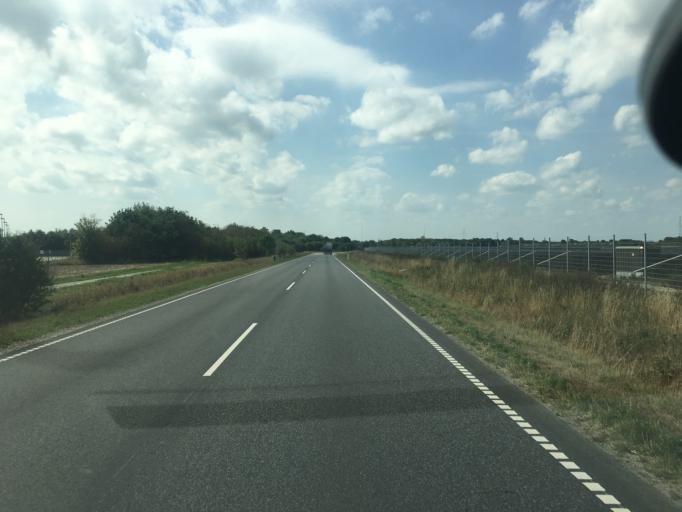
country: DK
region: South Denmark
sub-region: Aabenraa Kommune
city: Tinglev
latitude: 54.9470
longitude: 9.2731
